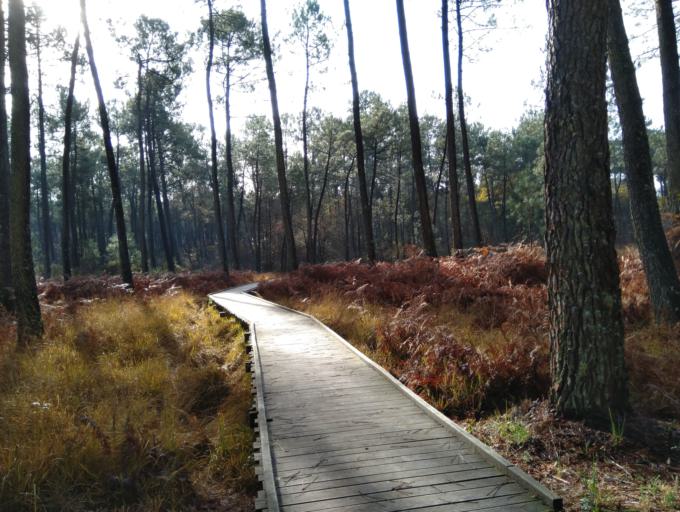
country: FR
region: Aquitaine
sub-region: Departement des Landes
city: Mees
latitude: 43.7056
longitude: -1.1222
